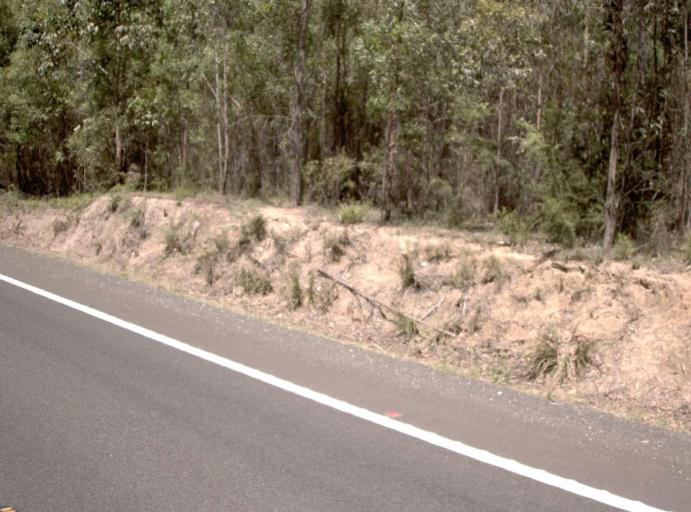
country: AU
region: New South Wales
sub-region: Bombala
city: Bombala
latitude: -37.5693
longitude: 149.0328
